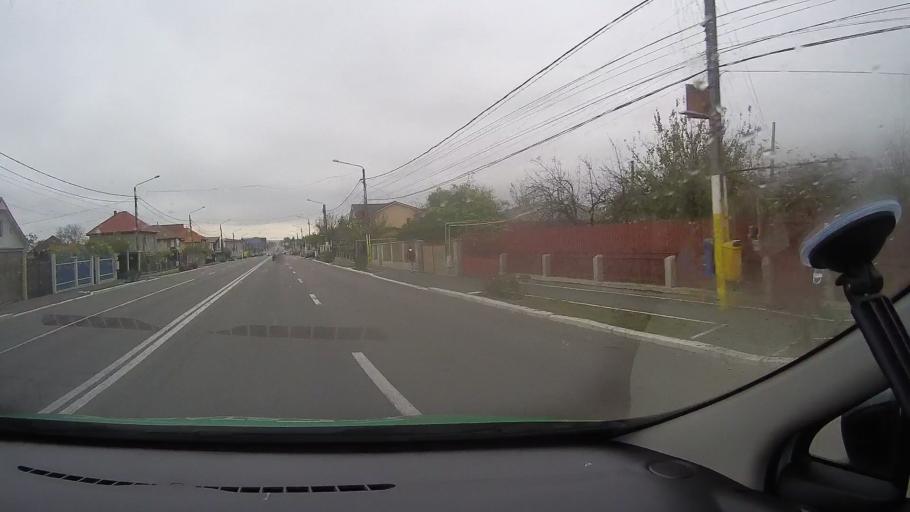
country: RO
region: Constanta
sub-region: Comuna Valu lui Traian
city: Valu lui Traian
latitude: 44.1649
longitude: 28.4706
